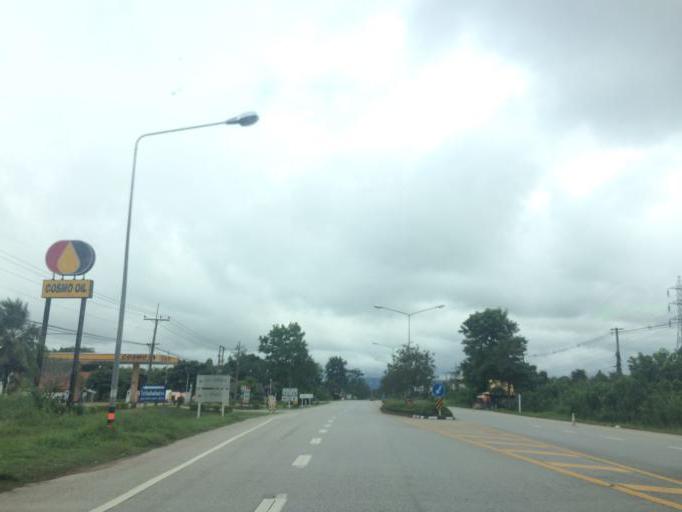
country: TH
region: Chiang Rai
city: Mae Lao
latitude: 19.7462
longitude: 99.6882
